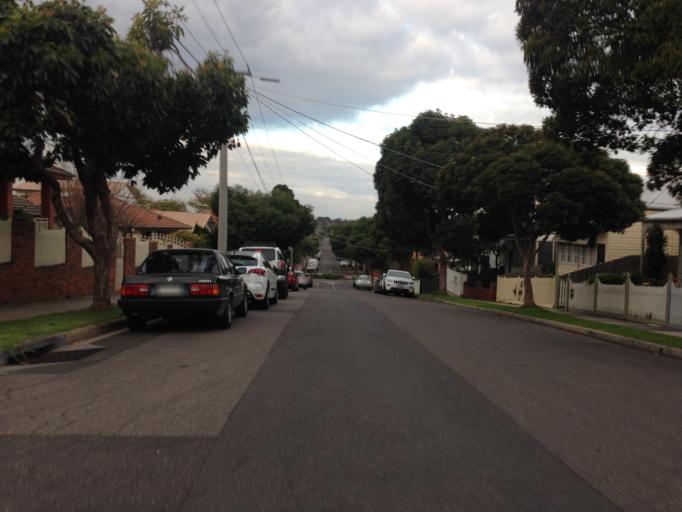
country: AU
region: Victoria
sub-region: Boroondara
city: Kew
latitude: -37.8000
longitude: 145.0365
